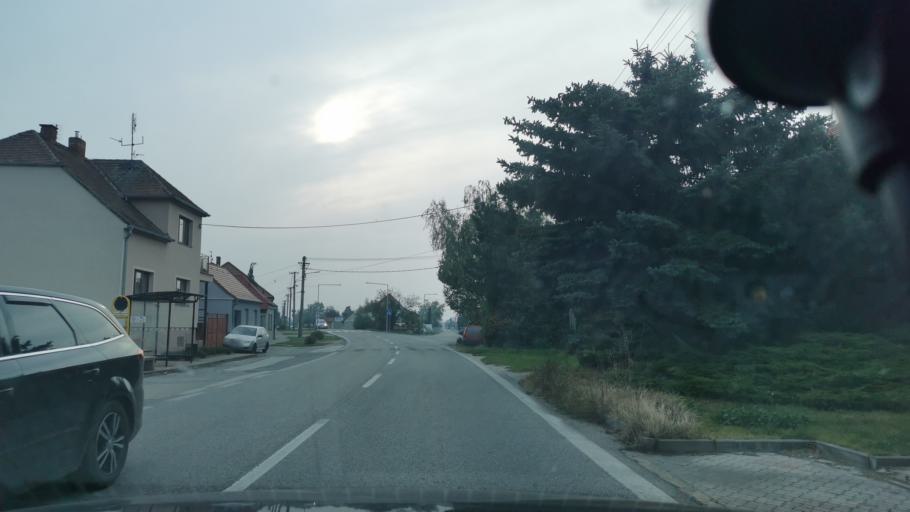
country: SK
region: Trnavsky
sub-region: Okres Skalica
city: Holic
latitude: 48.7900
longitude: 17.1230
